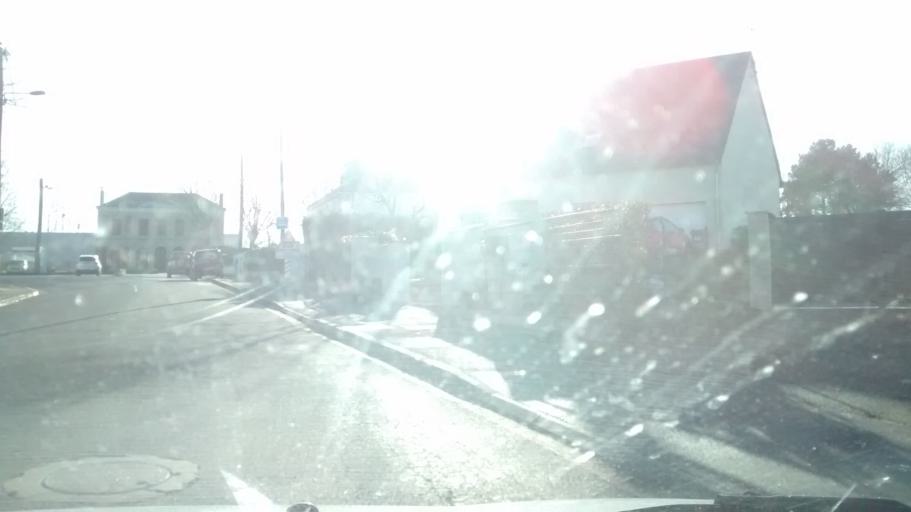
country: FR
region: Centre
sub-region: Departement d'Indre-et-Loire
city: Monnaie
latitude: 47.4997
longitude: 0.7921
